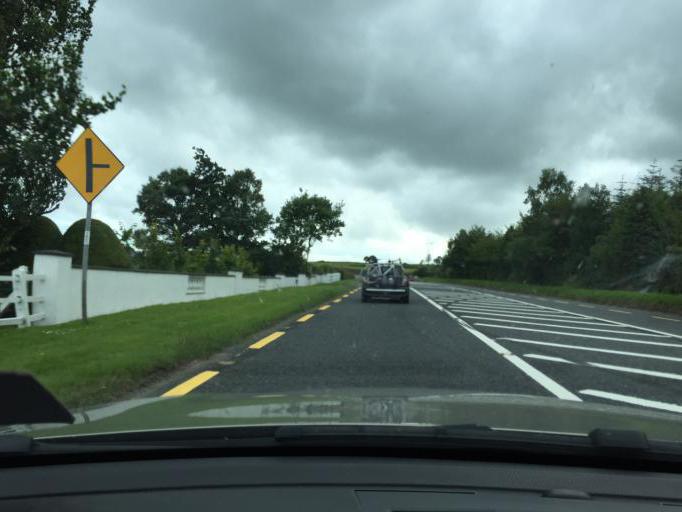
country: IE
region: Munster
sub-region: Waterford
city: Dungarvan
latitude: 52.1351
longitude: -7.5616
